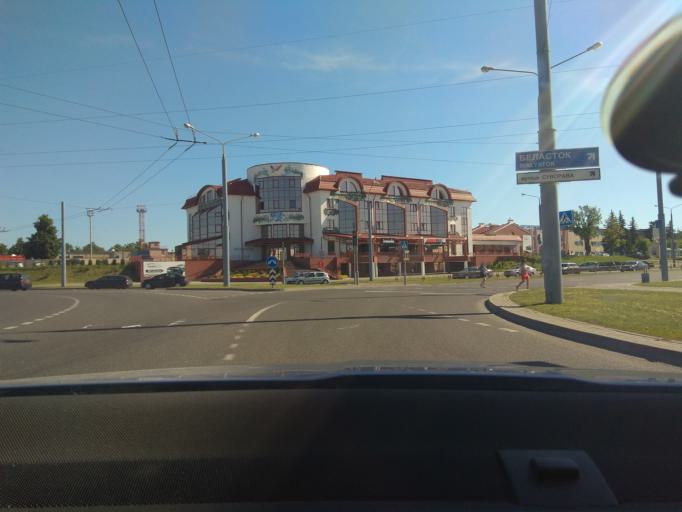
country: BY
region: Grodnenskaya
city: Hrodna
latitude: 53.6531
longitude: 23.7921
